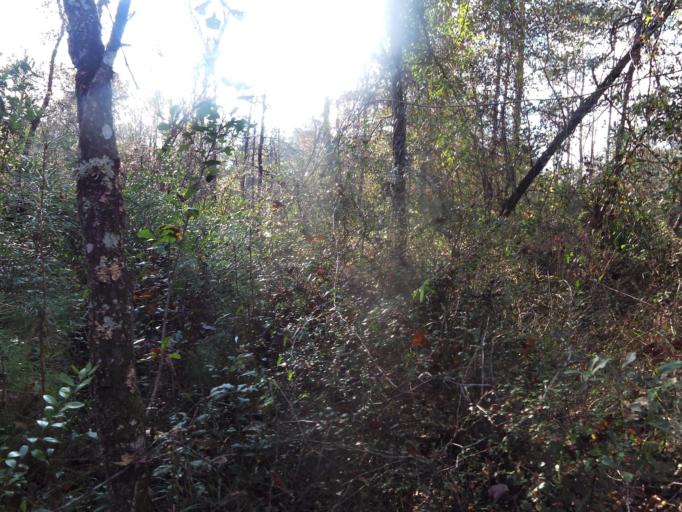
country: US
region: Florida
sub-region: Clay County
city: Middleburg
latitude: 30.1418
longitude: -81.9361
